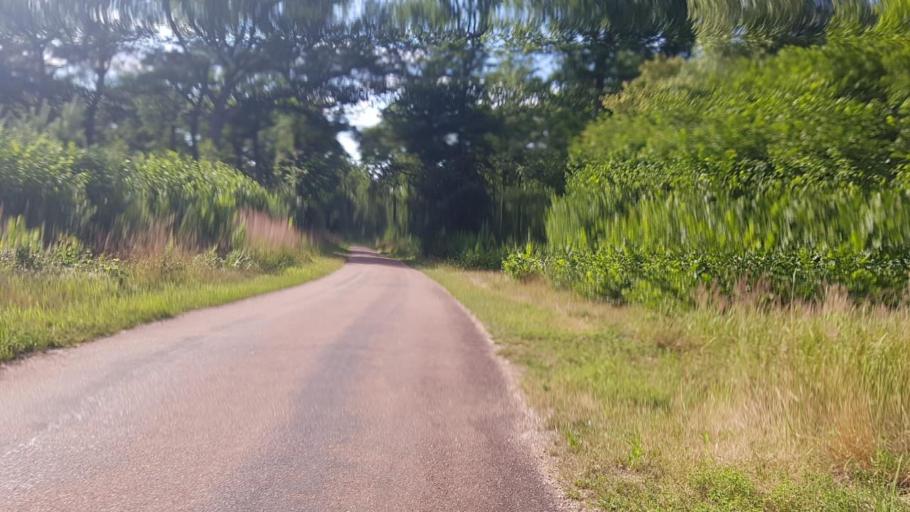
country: FR
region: Picardie
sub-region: Departement de l'Oise
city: Chamant
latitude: 49.1753
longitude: 2.6252
